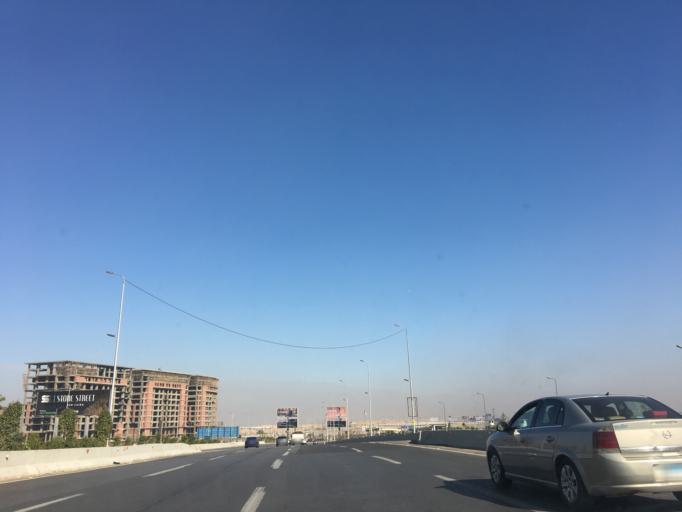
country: EG
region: Muhafazat al Qahirah
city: Cairo
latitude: 30.0448
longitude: 31.4058
